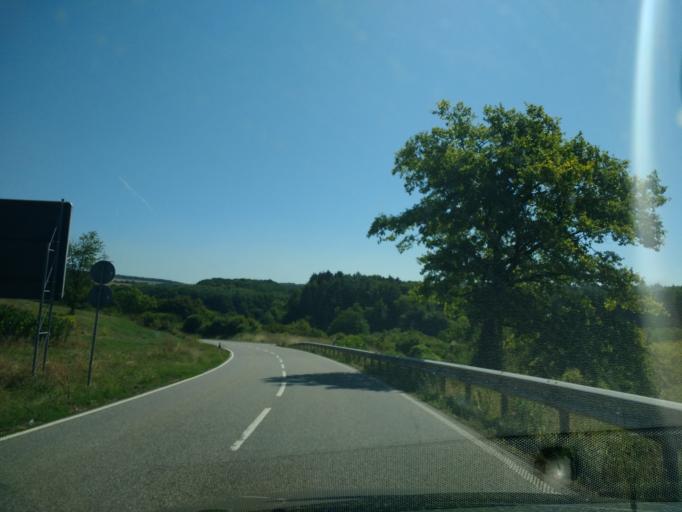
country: LU
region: Grevenmacher
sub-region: Canton de Grevenmacher
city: Wormeldange
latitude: 49.5827
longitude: 6.3945
